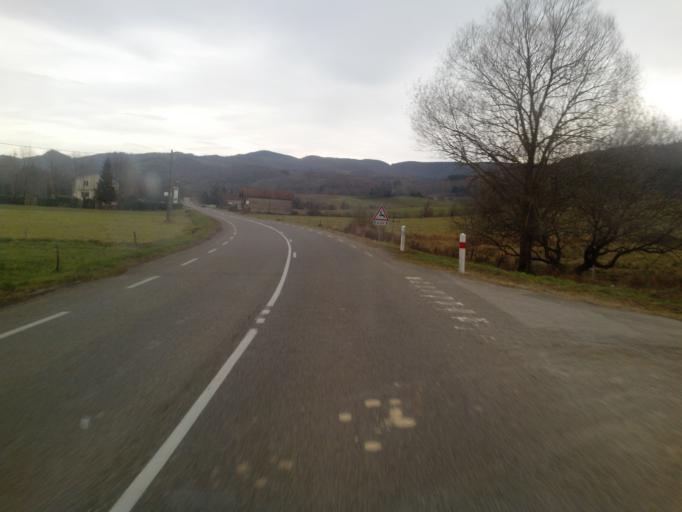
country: FR
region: Midi-Pyrenees
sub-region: Departement de l'Ariege
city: Foix
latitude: 43.0136
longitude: 1.4065
